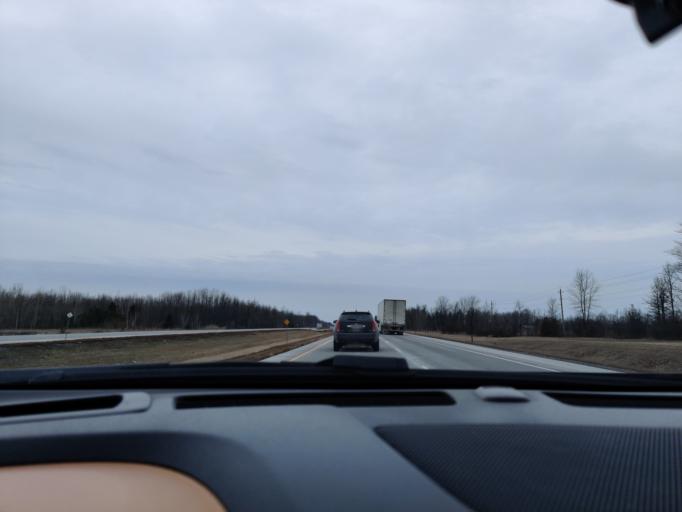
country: US
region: New York
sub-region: St. Lawrence County
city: Norfolk
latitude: 44.9378
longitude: -75.1493
